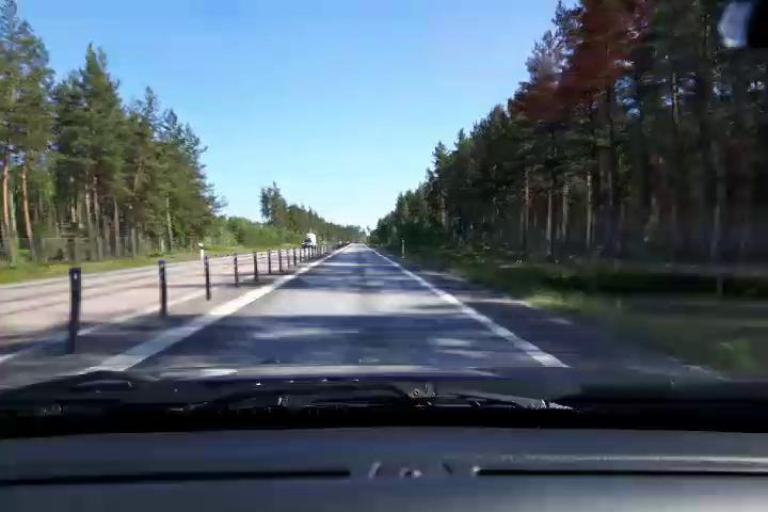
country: SE
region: Gaevleborg
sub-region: Gavle Kommun
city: Norrsundet
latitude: 60.9921
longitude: 17.0024
